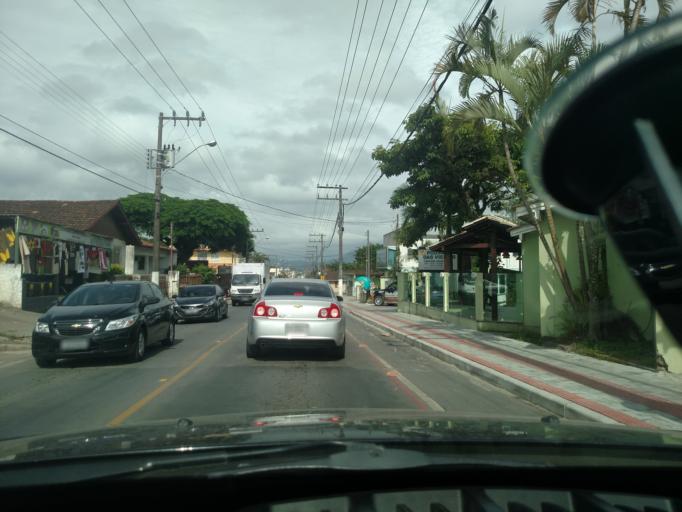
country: BR
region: Santa Catarina
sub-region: Porto Belo
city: Porto Belo
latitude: -27.1571
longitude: -48.5579
